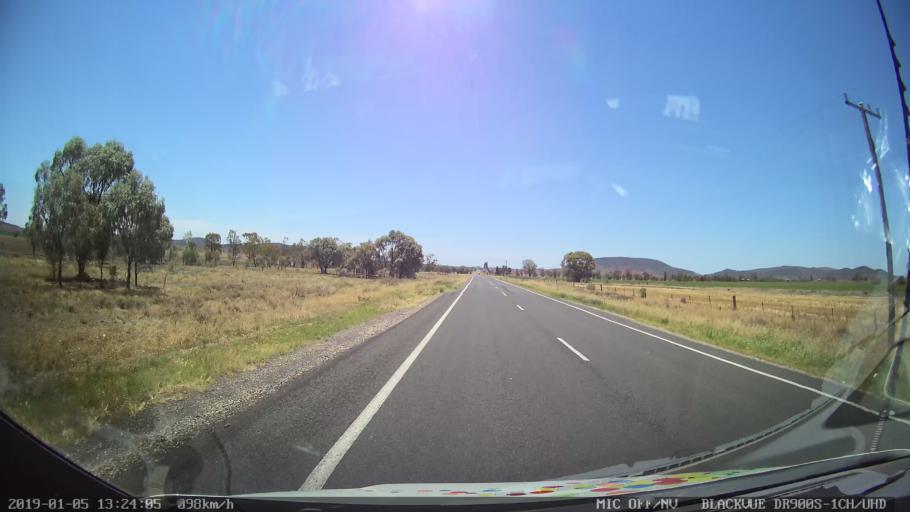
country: AU
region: New South Wales
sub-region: Gunnedah
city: Gunnedah
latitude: -31.0725
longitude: 149.9841
